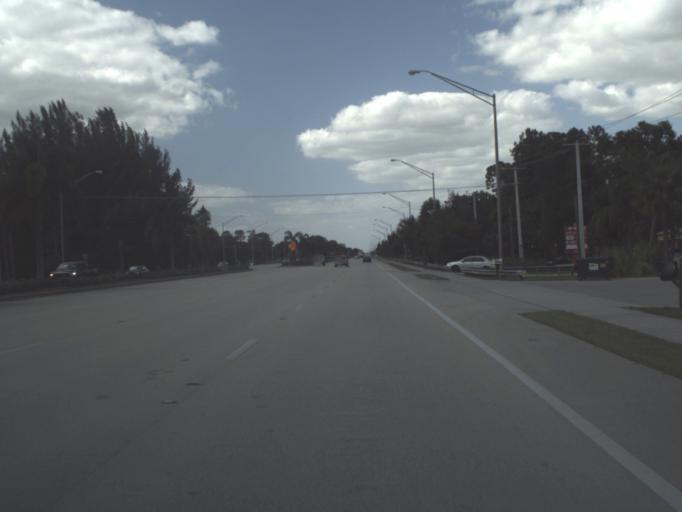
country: US
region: Florida
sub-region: Collier County
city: Naples Manor
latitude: 26.0847
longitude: -81.7273
